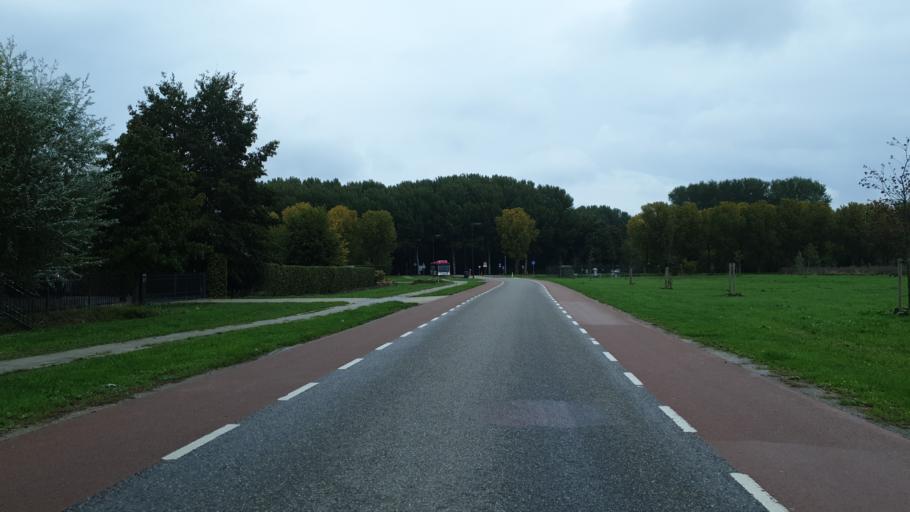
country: NL
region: Gelderland
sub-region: Gemeente Beuningen
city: Beuningen
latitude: 51.8516
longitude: 5.7792
